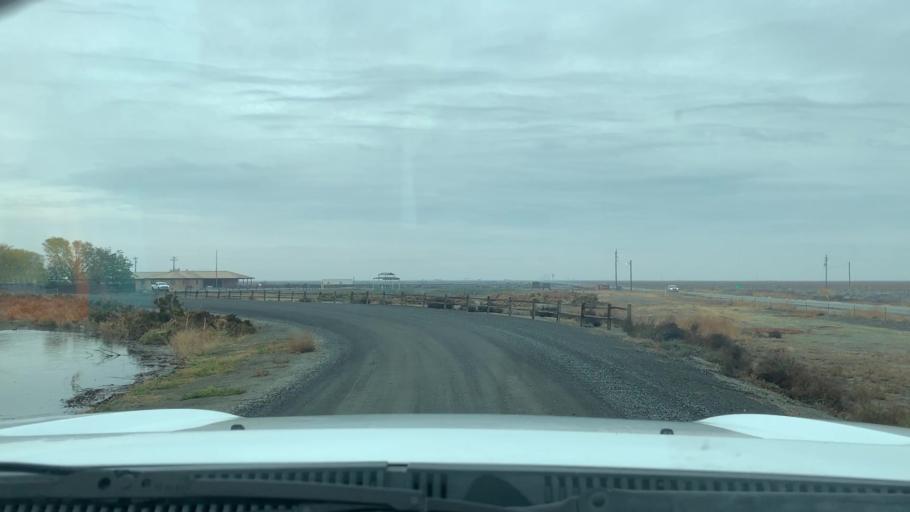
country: US
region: California
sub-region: Tulare County
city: Alpaugh
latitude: 35.7585
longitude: -119.5799
